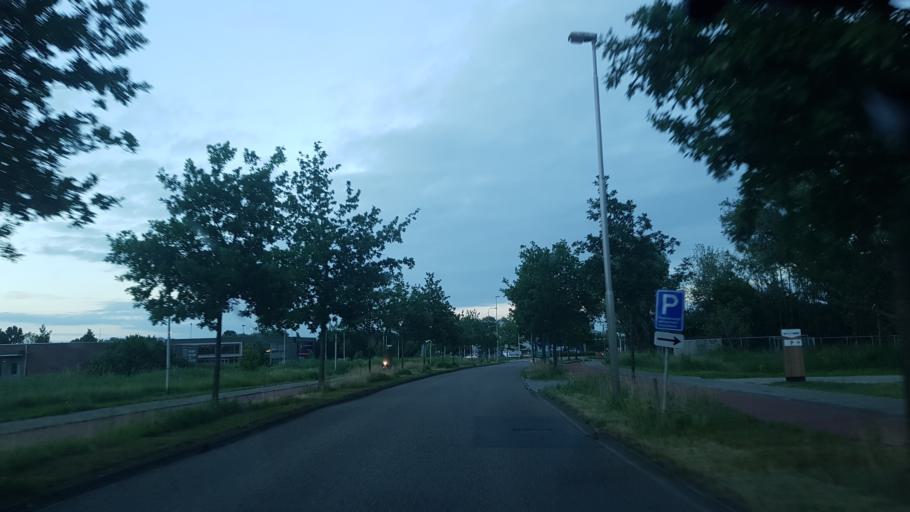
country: NL
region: Friesland
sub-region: Gemeente Leeuwarden
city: Camminghaburen
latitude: 53.2104
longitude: 5.8258
